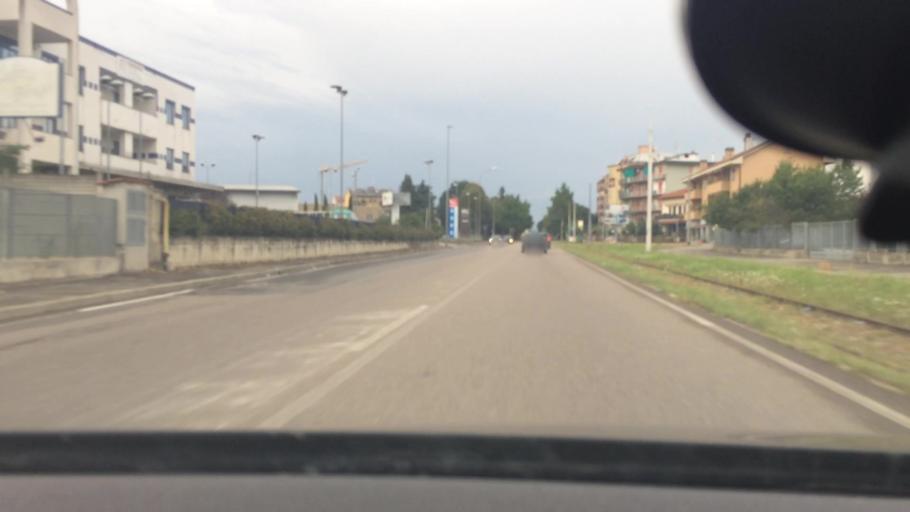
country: IT
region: Lombardy
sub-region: Provincia di Monza e Brianza
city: Nova Milanese
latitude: 45.5796
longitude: 9.1937
